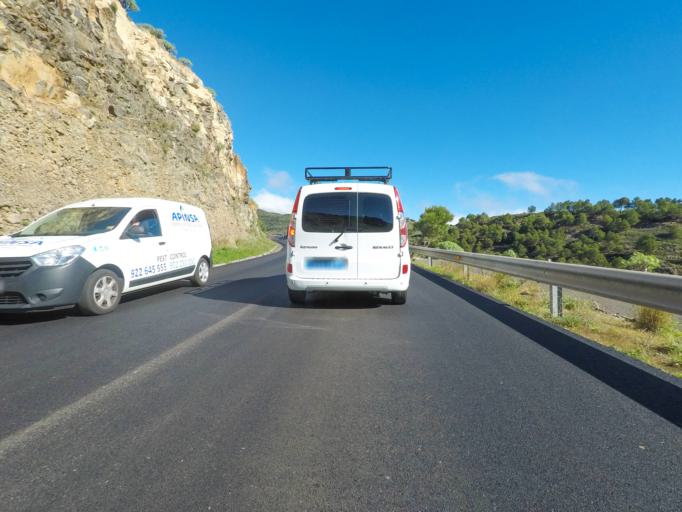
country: ES
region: Canary Islands
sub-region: Provincia de Santa Cruz de Tenerife
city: Alajero
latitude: 28.0863
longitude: -17.1999
